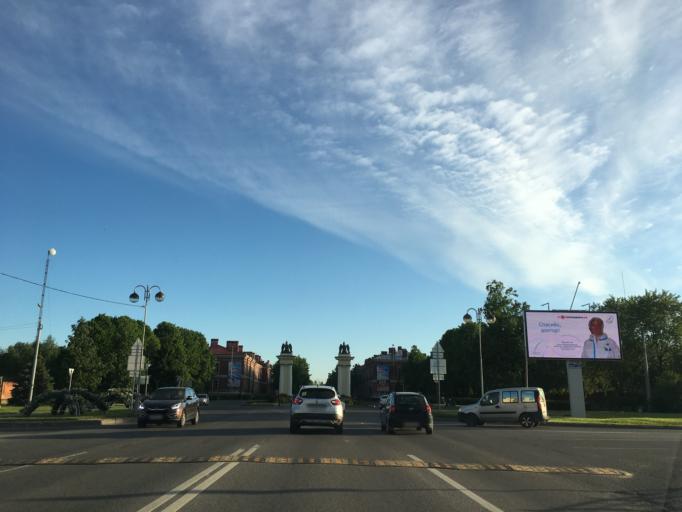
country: RU
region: Leningrad
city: Gatchina
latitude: 59.5772
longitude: 30.1333
